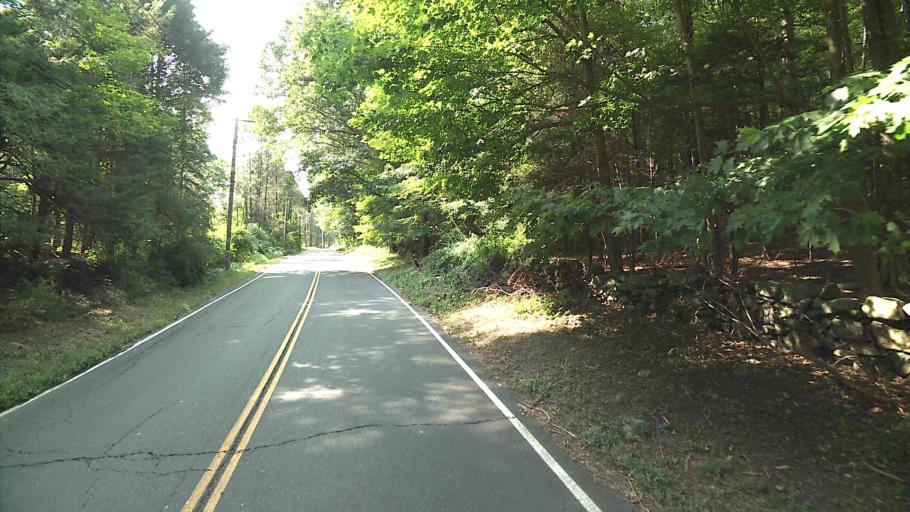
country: US
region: Connecticut
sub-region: Fairfield County
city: Westport
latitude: 41.2392
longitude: -73.3210
